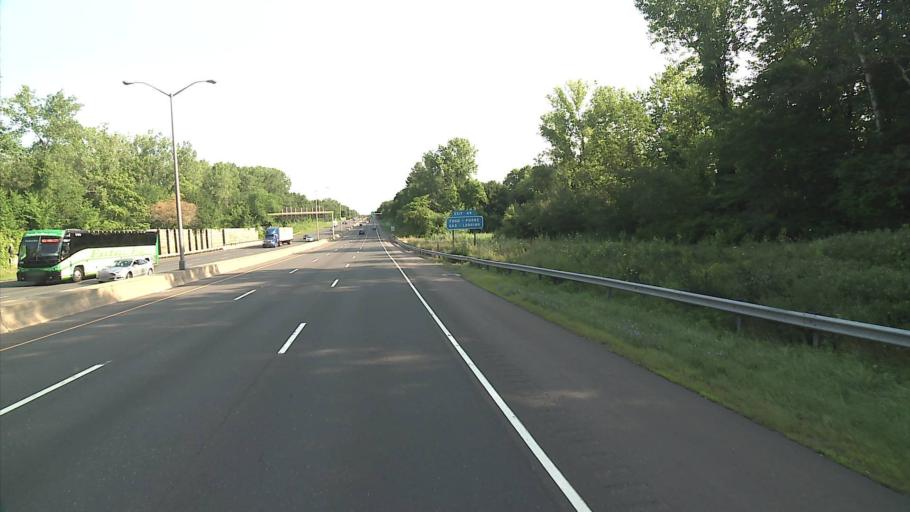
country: US
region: Connecticut
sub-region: Hartford County
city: Thompsonville
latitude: 42.0061
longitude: -72.5853
